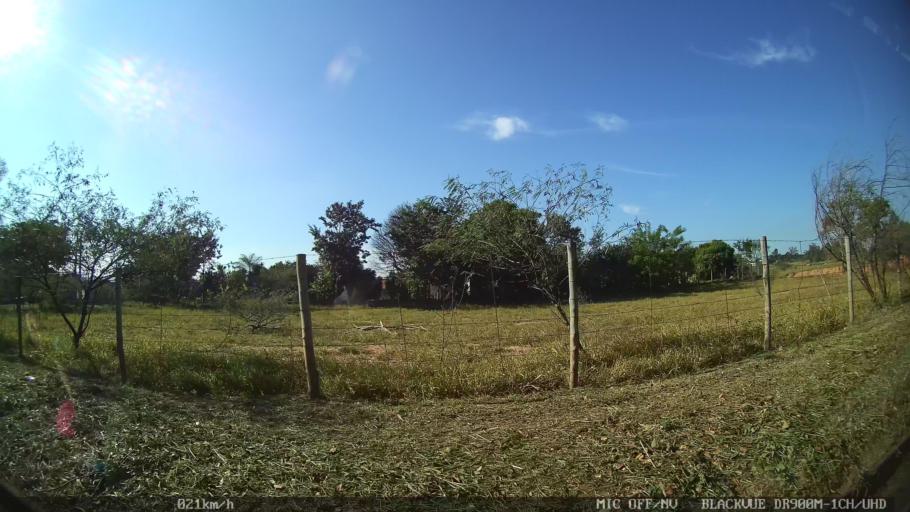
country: BR
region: Sao Paulo
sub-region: Campinas
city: Campinas
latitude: -22.9676
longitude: -47.1102
